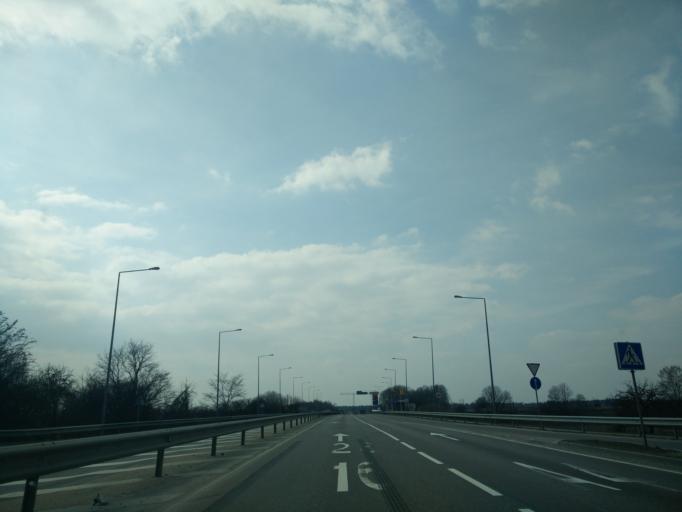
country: LT
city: Lentvaris
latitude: 54.6235
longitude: 25.1091
